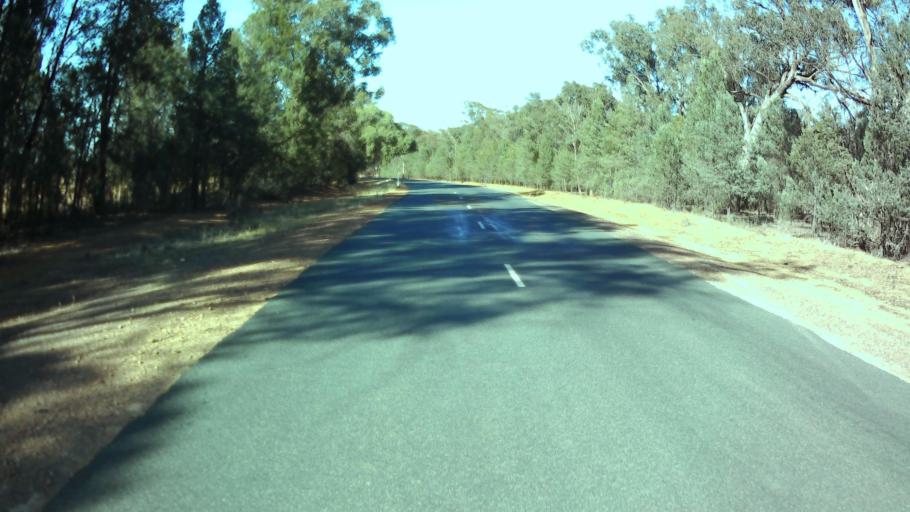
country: AU
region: New South Wales
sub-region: Weddin
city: Grenfell
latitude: -34.0133
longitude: 148.1135
